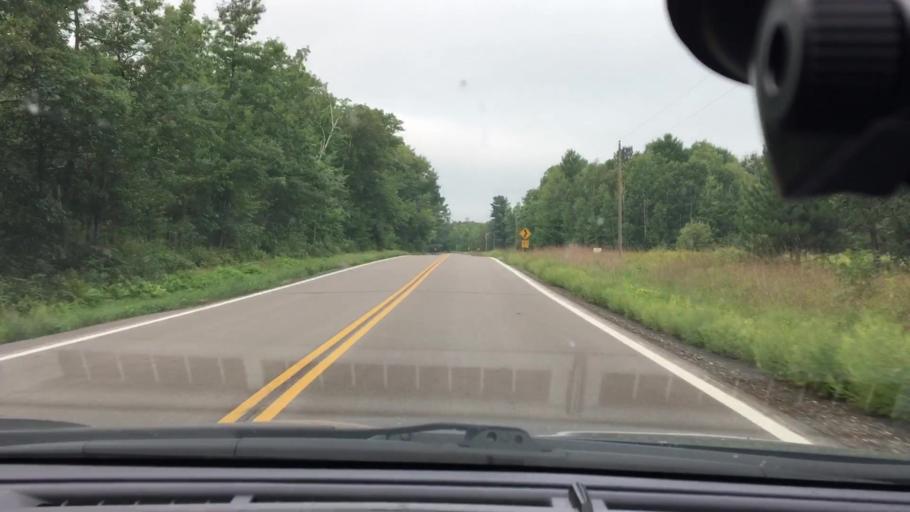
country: US
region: Minnesota
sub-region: Crow Wing County
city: Cross Lake
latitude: 46.6622
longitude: -93.9576
